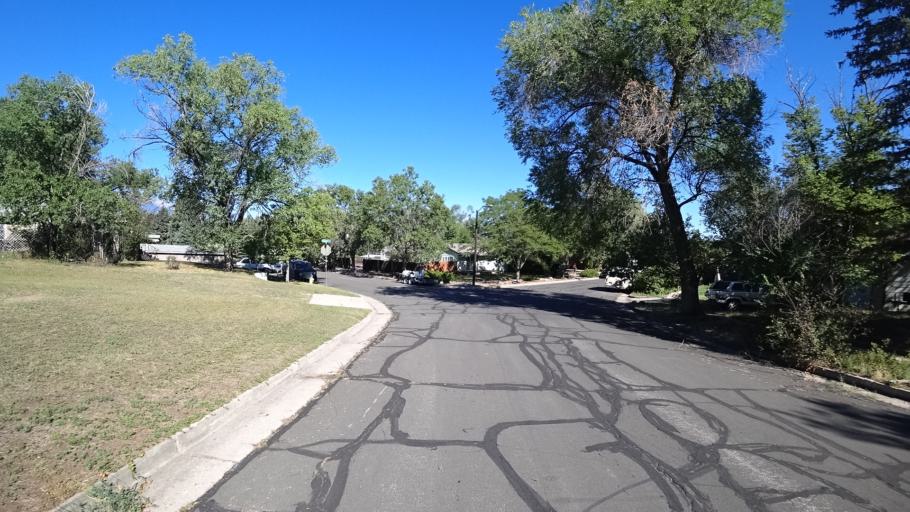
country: US
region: Colorado
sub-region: El Paso County
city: Colorado Springs
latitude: 38.8514
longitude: -104.7825
